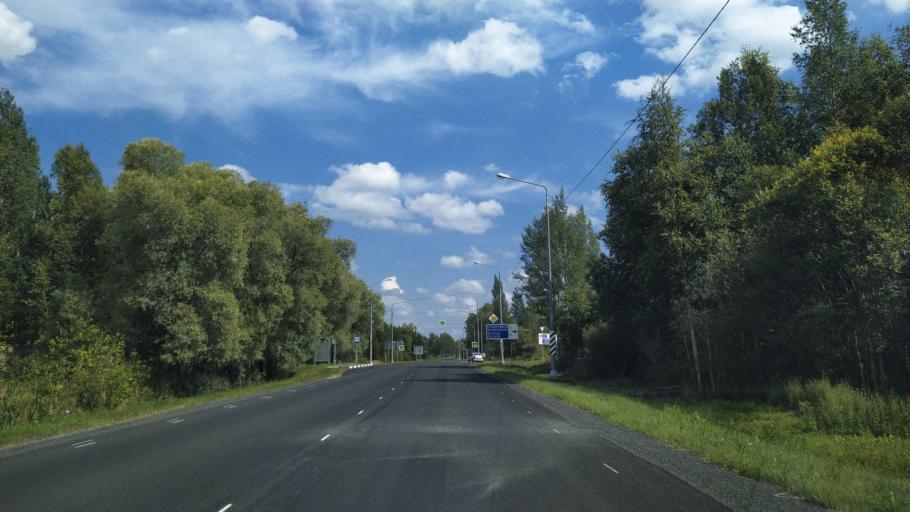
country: RU
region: Pskov
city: Porkhov
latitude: 57.7278
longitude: 29.1570
